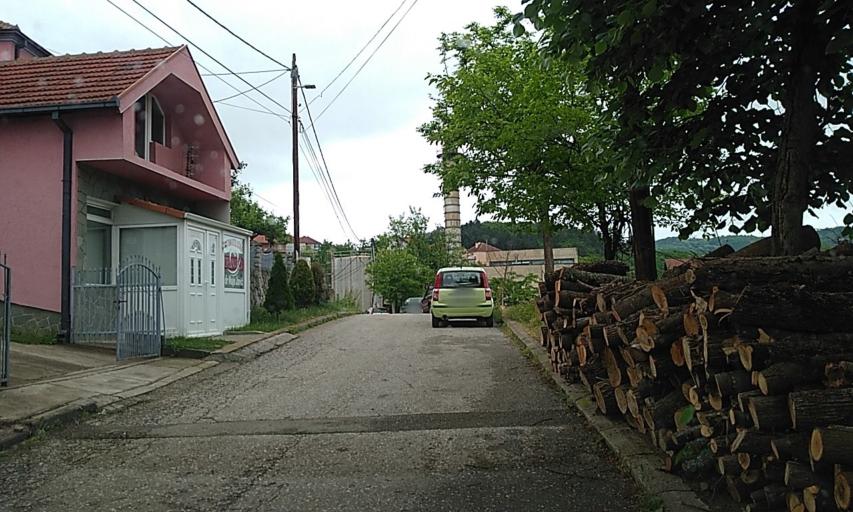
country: RS
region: Central Serbia
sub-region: Pcinjski Okrug
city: Vladicin Han
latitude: 42.7145
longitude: 22.0634
